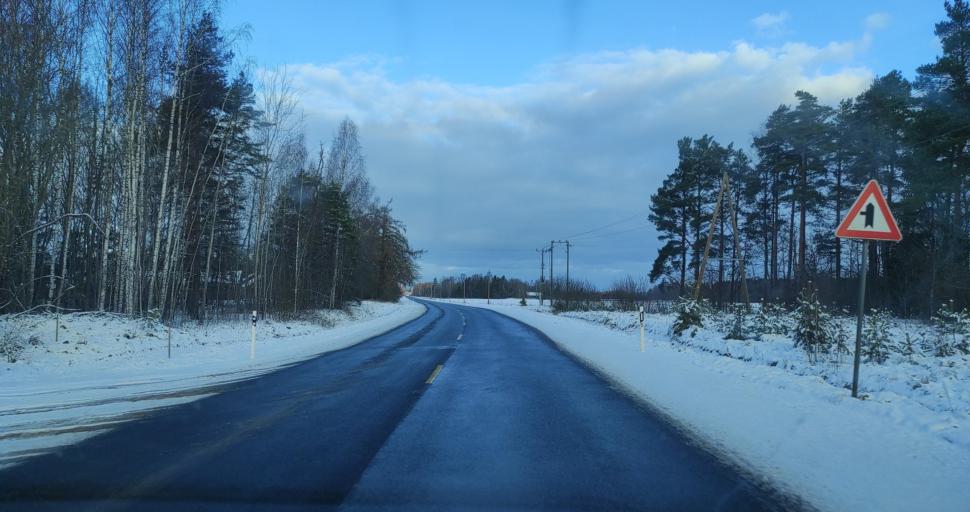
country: LV
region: Skrunda
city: Skrunda
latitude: 56.7338
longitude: 22.0006
